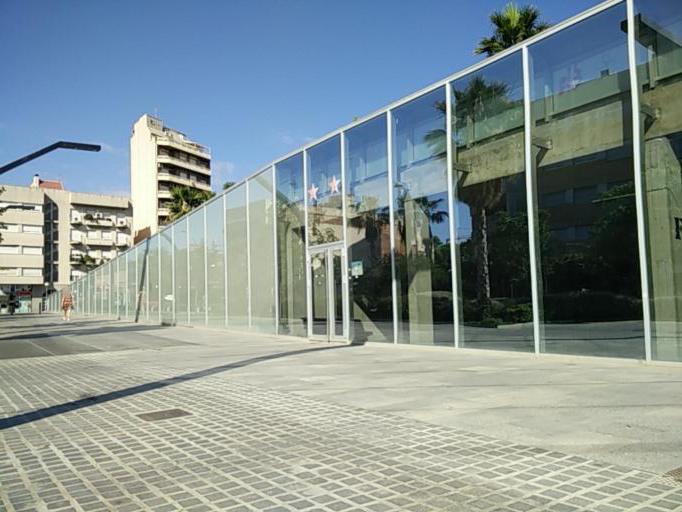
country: ES
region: Catalonia
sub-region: Provincia de Barcelona
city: Badalona
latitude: 41.4485
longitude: 2.2435
